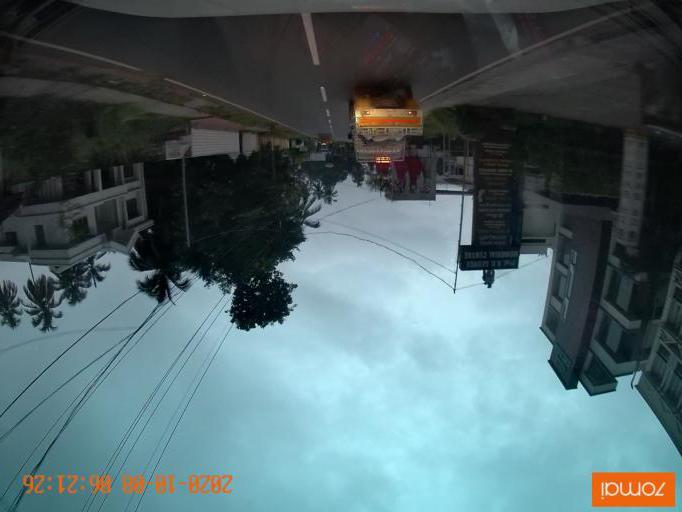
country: IN
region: Kerala
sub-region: Thrissur District
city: Trichur
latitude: 10.5208
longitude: 76.2317
